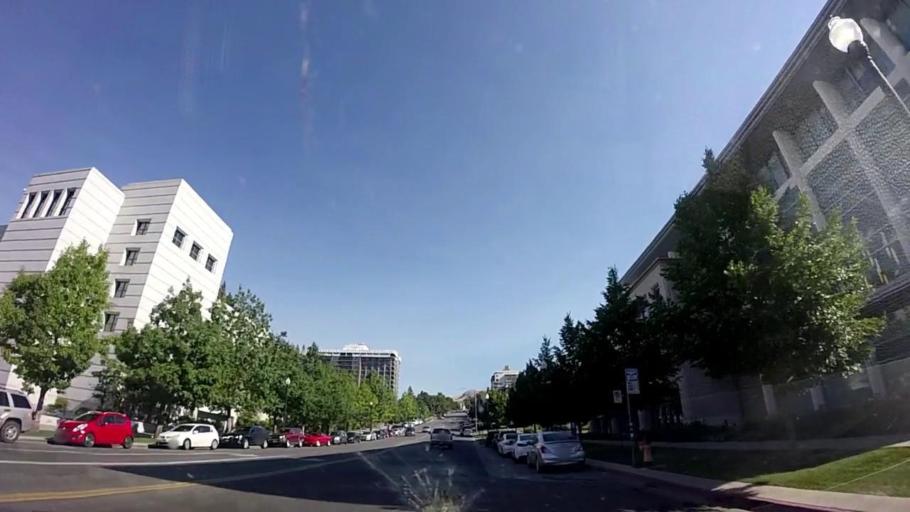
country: US
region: Utah
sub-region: Salt Lake County
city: Salt Lake City
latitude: 40.7719
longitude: -111.8910
